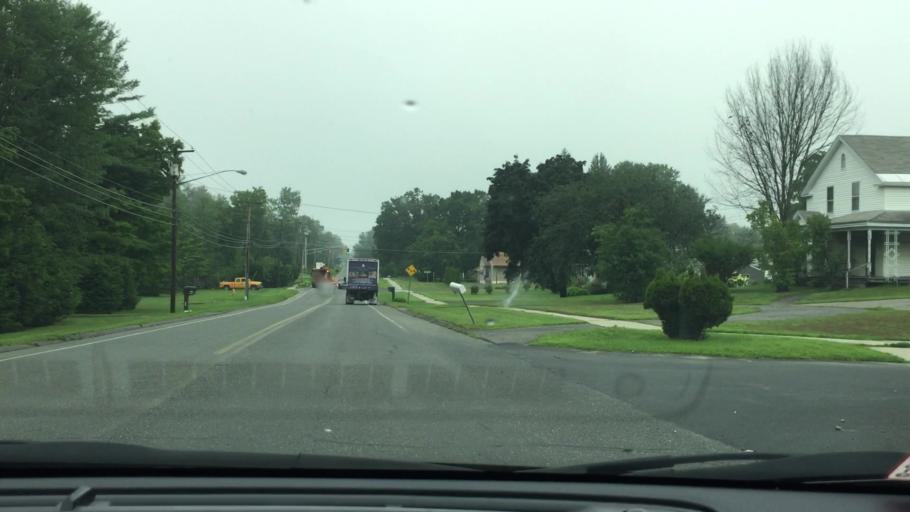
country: US
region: Massachusetts
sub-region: Berkshire County
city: Pittsfield
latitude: 42.4307
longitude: -73.2028
